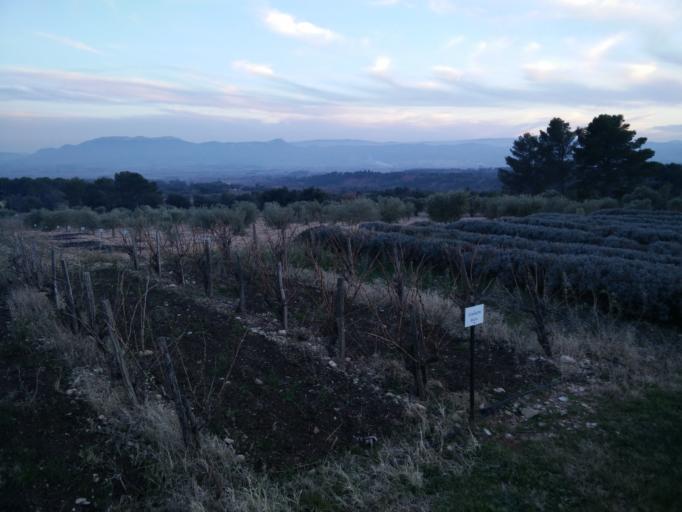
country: FR
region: Provence-Alpes-Cote d'Azur
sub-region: Departement des Bouches-du-Rhone
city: Puyloubier
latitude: 43.5266
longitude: 5.6498
